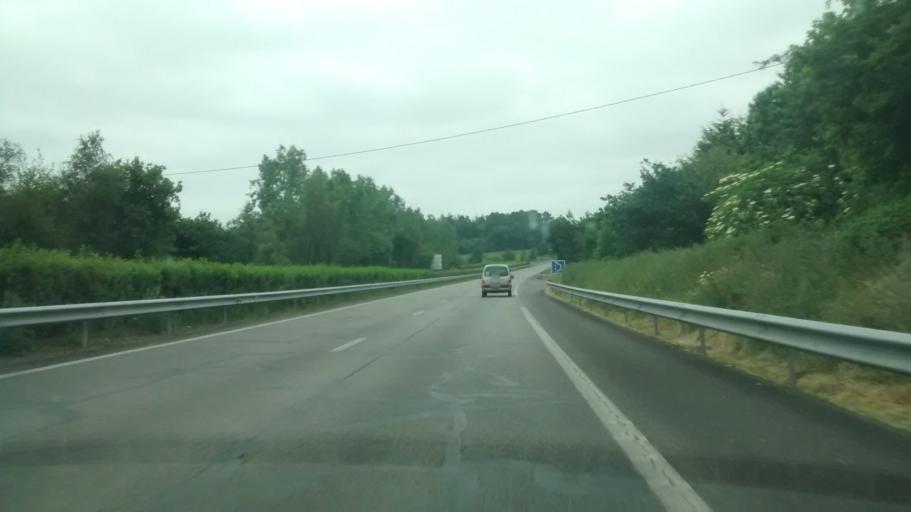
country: FR
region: Brittany
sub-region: Departement du Morbihan
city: Serent
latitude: 47.7918
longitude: -2.4532
